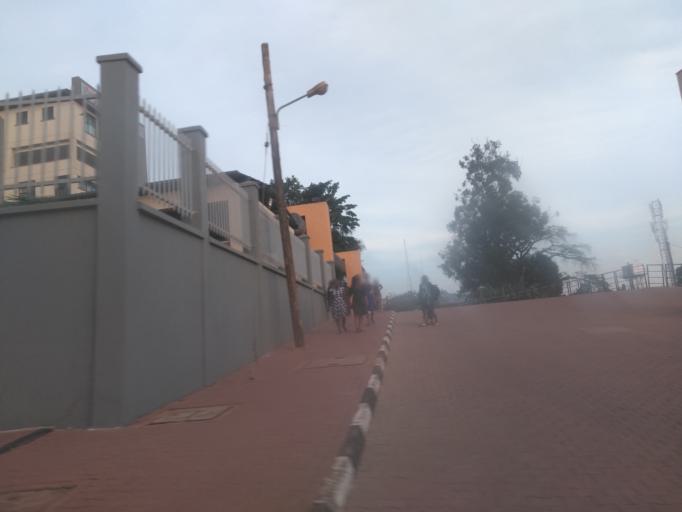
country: UG
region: Central Region
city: Kampala Central Division
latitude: 0.3376
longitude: 32.5774
